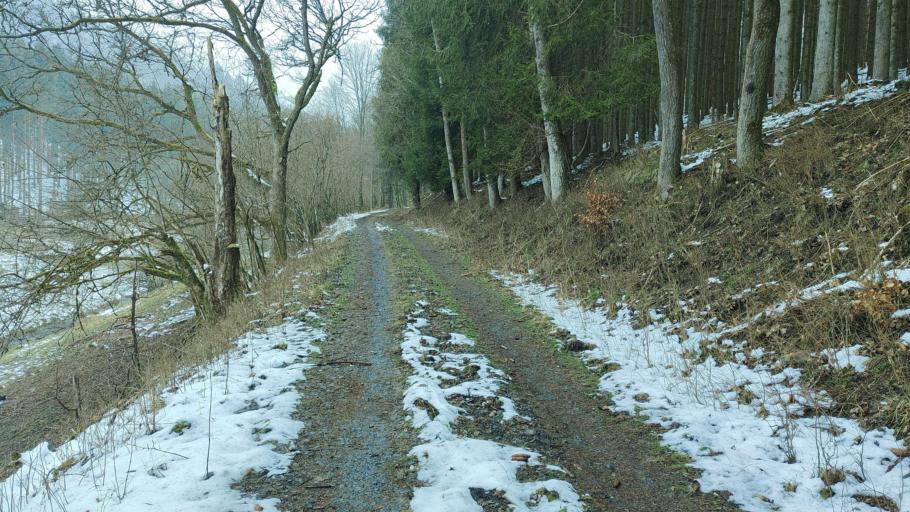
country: DE
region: North Rhine-Westphalia
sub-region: Regierungsbezirk Arnsberg
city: Bad Berleburg
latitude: 51.1089
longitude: 8.4308
